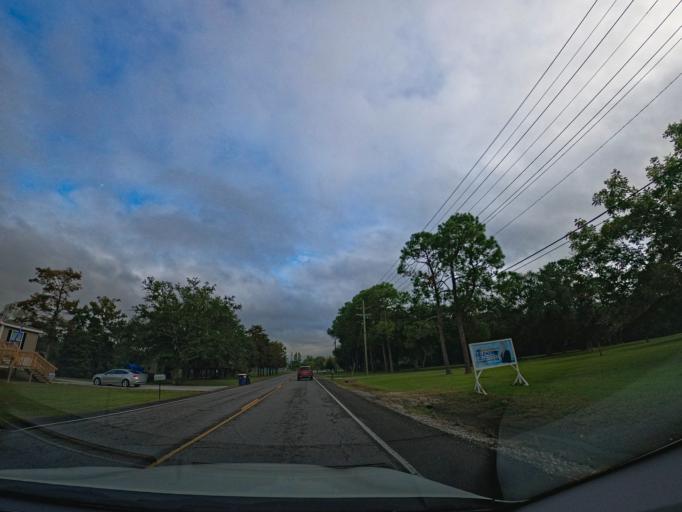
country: US
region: Louisiana
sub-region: Terrebonne Parish
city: Dulac
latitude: 29.4760
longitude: -90.7009
